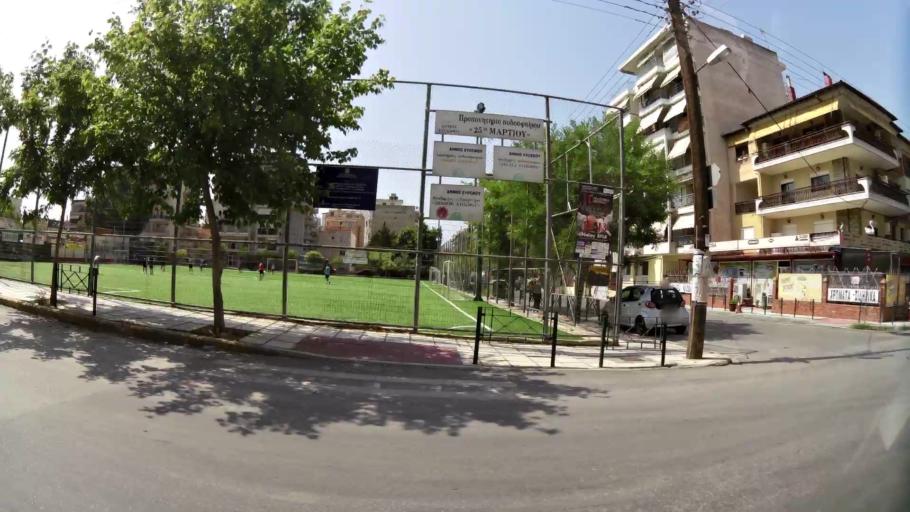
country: GR
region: Central Macedonia
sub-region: Nomos Thessalonikis
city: Evosmos
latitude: 40.6727
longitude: 22.9180
